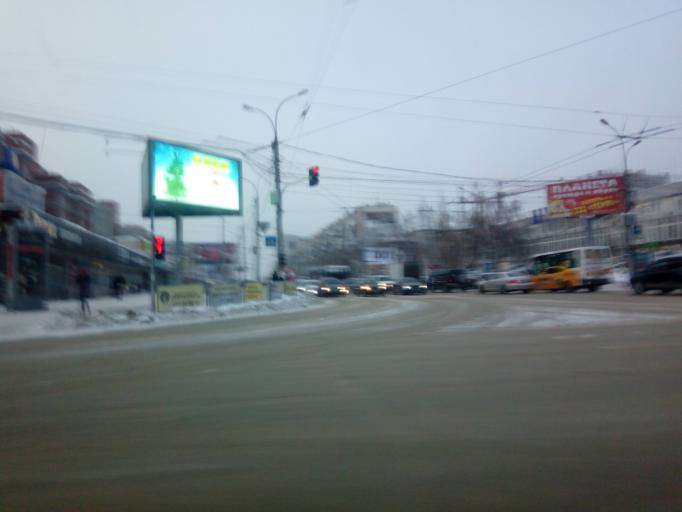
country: RU
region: Novosibirsk
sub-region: Novosibirskiy Rayon
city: Novosibirsk
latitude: 55.0324
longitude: 82.9103
